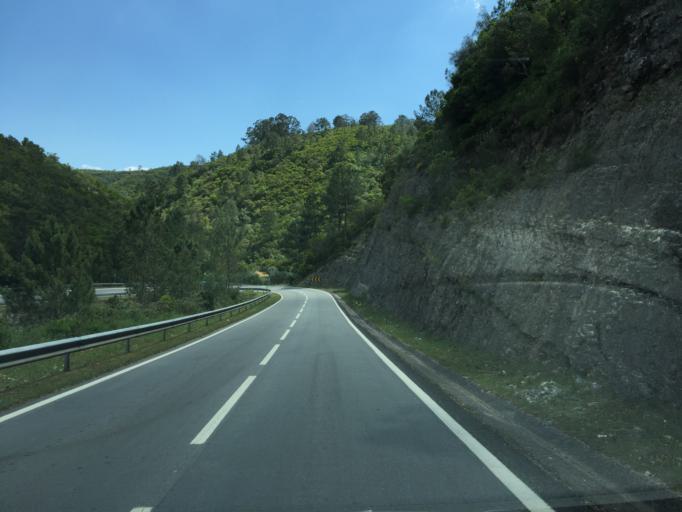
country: PT
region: Santarem
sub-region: Ourem
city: Fatima
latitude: 39.6327
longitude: -8.6523
